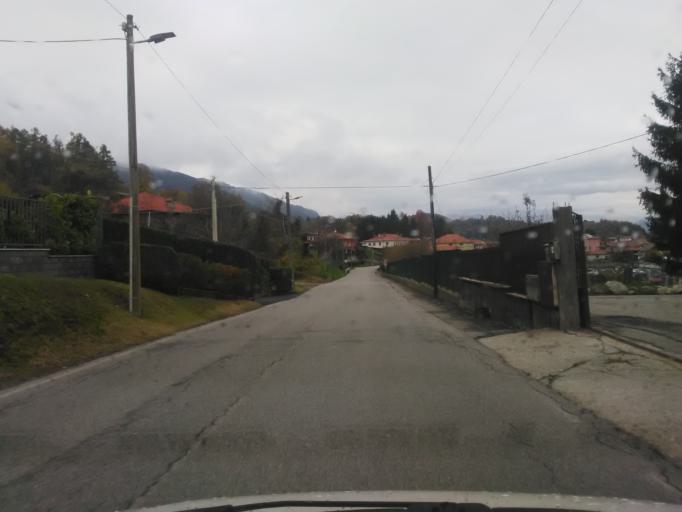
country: IT
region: Piedmont
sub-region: Provincia di Novara
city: Pogno
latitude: 45.7532
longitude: 8.3807
